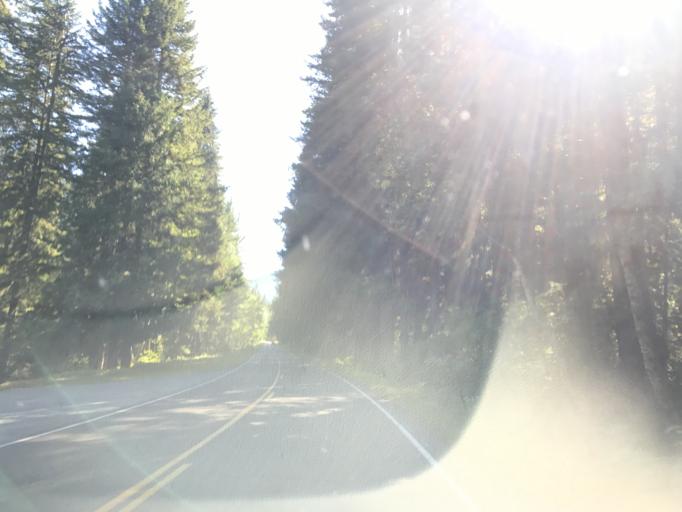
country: US
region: Washington
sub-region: Pierce County
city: Buckley
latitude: 46.7645
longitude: -121.6377
